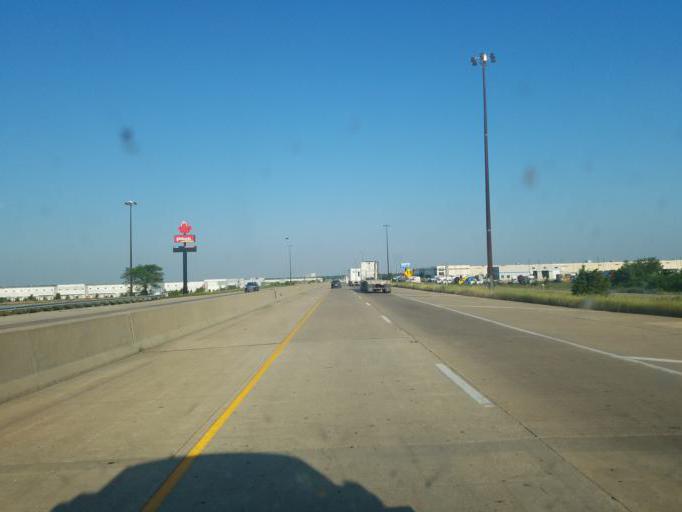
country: US
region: Illinois
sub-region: Grundy County
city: Minooka
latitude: 41.4623
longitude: -88.2718
